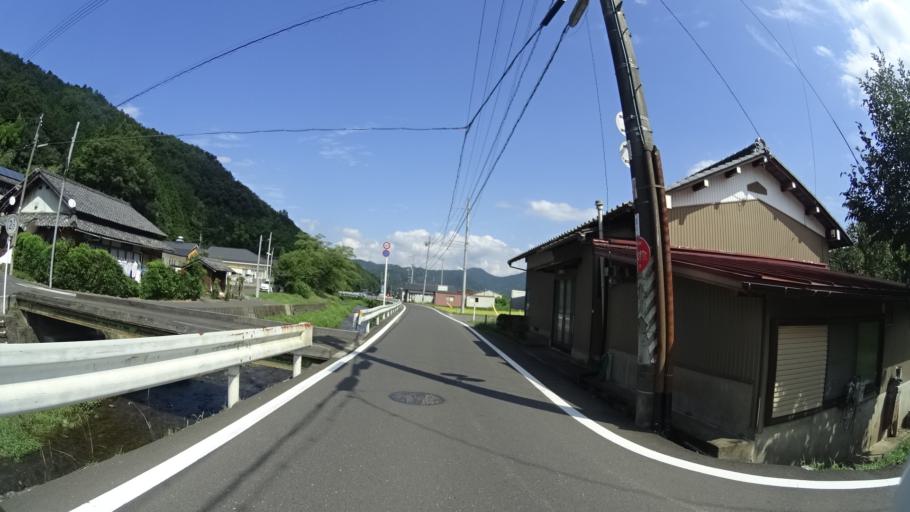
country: JP
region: Kyoto
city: Maizuru
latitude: 35.4318
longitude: 135.3106
